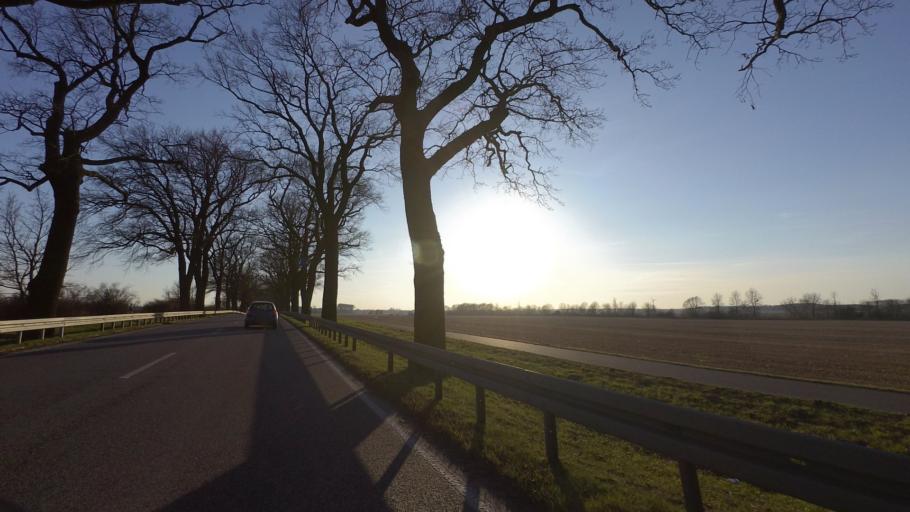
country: DE
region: Brandenburg
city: Werneuchen
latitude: 52.6293
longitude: 13.7175
